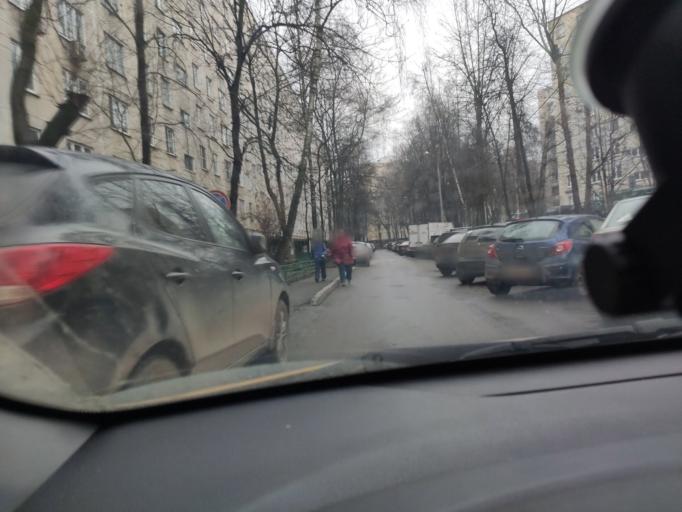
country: RU
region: Moscow
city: Chertanovo Yuzhnoye
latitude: 55.6089
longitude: 37.6000
